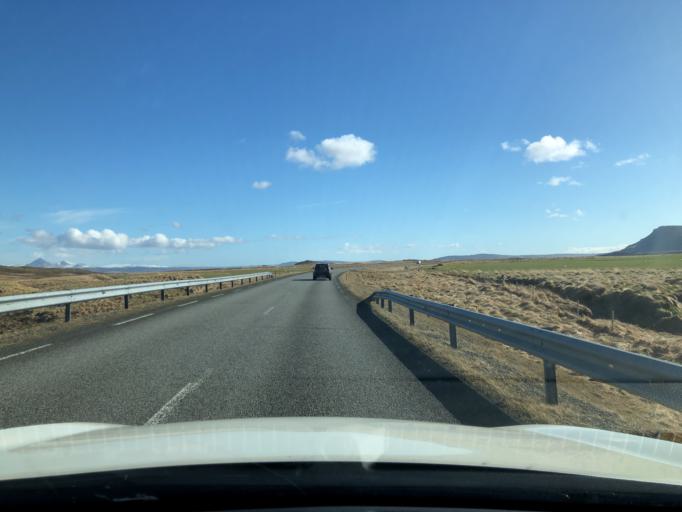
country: IS
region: West
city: Borgarnes
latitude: 64.5801
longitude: -21.6477
